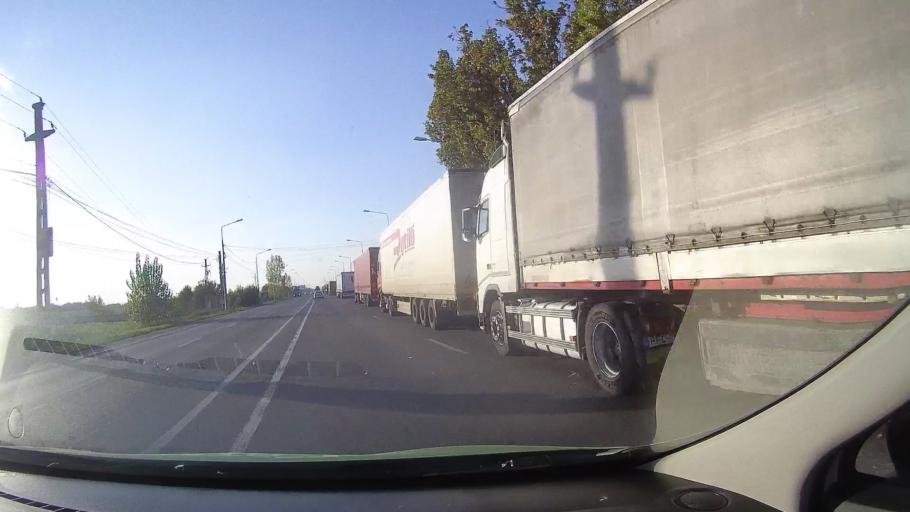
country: RO
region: Bihor
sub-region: Comuna Bors
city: Santion
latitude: 47.1024
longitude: 21.8388
